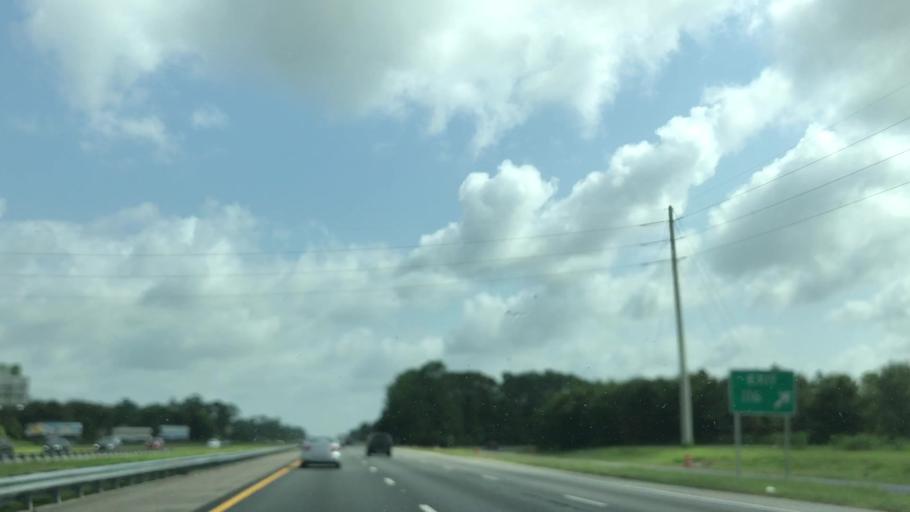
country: US
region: Florida
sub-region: Volusia County
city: Lake Helen
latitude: 28.9839
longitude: -81.2480
